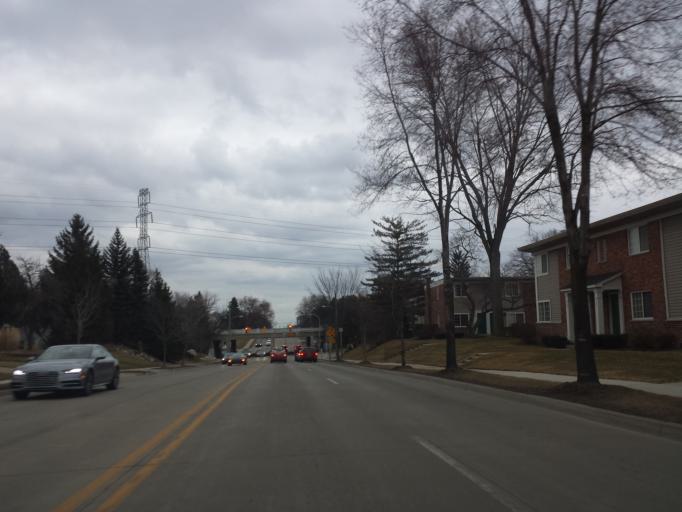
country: US
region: Michigan
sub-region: Oakland County
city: Birmingham
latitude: 42.5472
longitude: -83.1978
